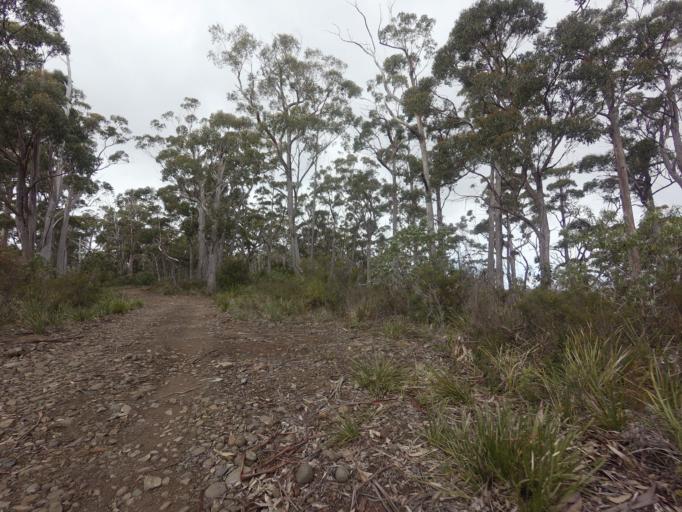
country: AU
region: Tasmania
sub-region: Huon Valley
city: Geeveston
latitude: -43.4623
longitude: 146.9165
